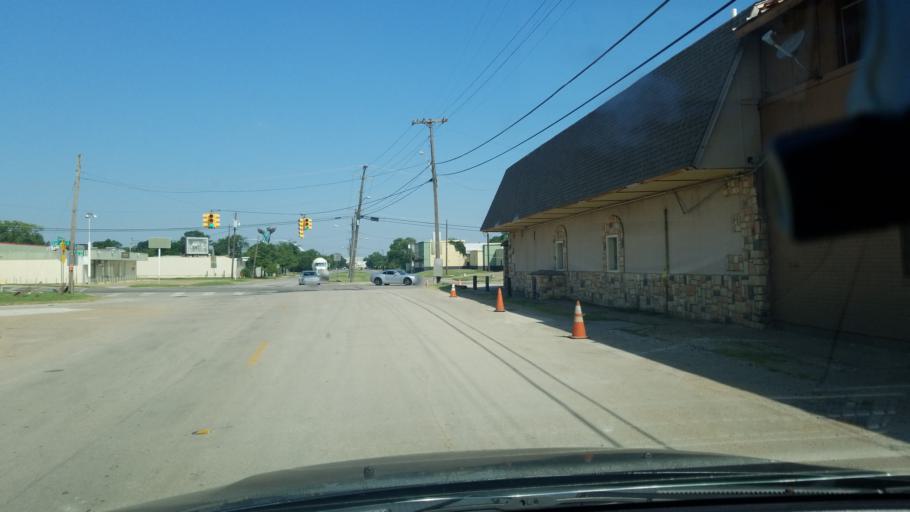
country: US
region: Texas
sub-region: Dallas County
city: Dallas
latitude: 32.7595
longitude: -96.7934
